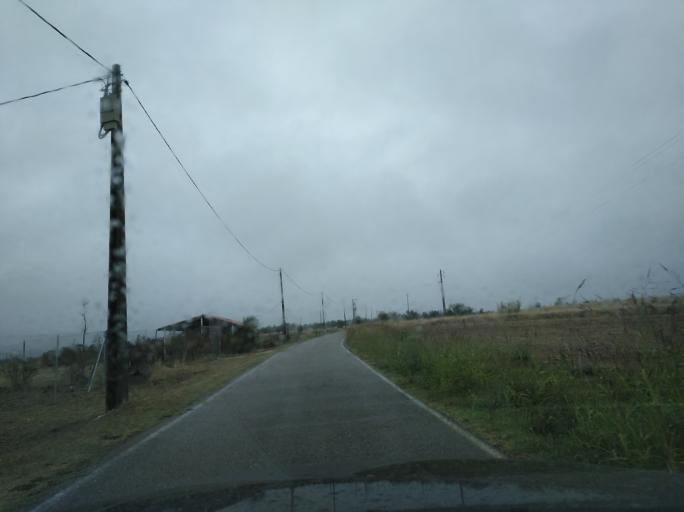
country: PT
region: Portalegre
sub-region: Campo Maior
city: Campo Maior
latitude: 38.9544
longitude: -7.0846
